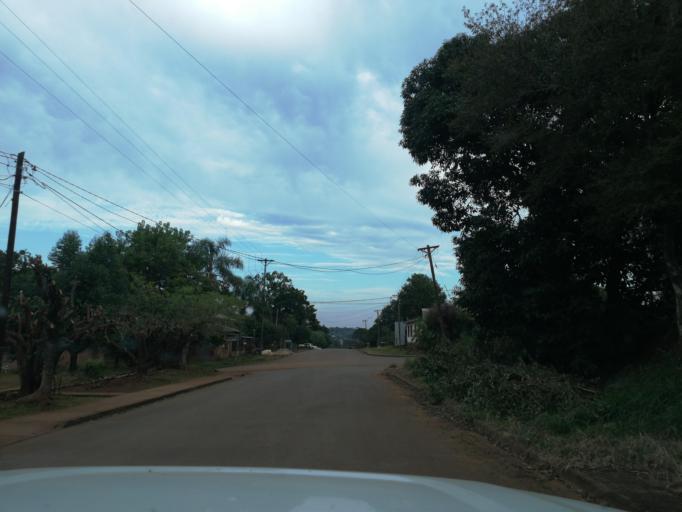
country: AR
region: Misiones
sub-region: Departamento de San Pedro
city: San Pedro
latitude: -26.6264
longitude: -54.1022
